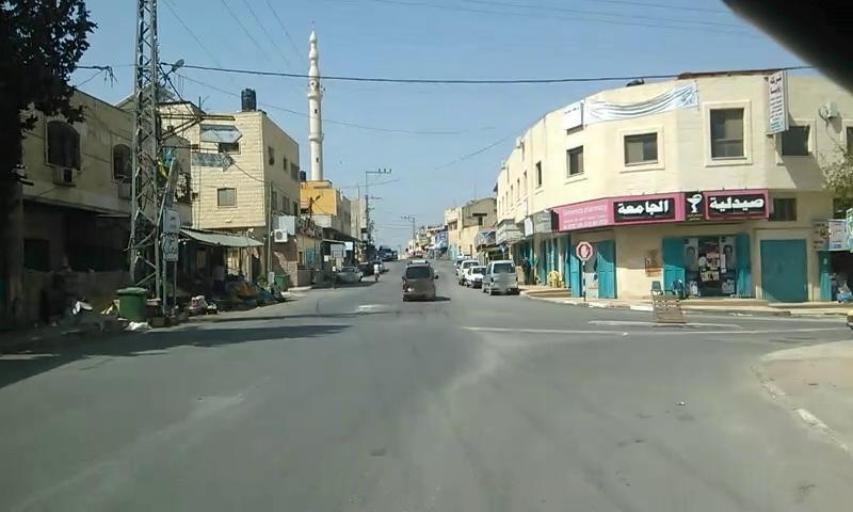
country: PS
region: West Bank
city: Az Zababidah
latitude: 32.3844
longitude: 35.3254
